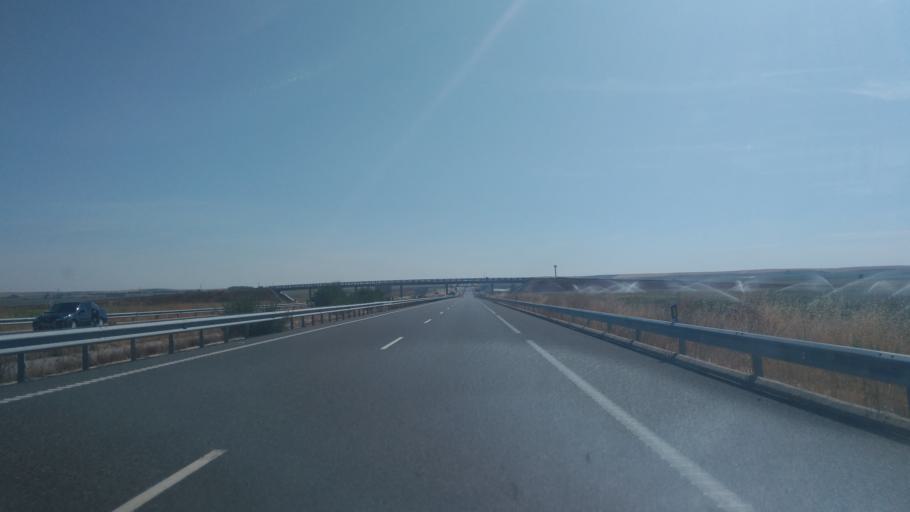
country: ES
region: Castille and Leon
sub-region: Provincia de Salamanca
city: Encinas de Abajo
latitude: 40.9308
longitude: -5.4483
